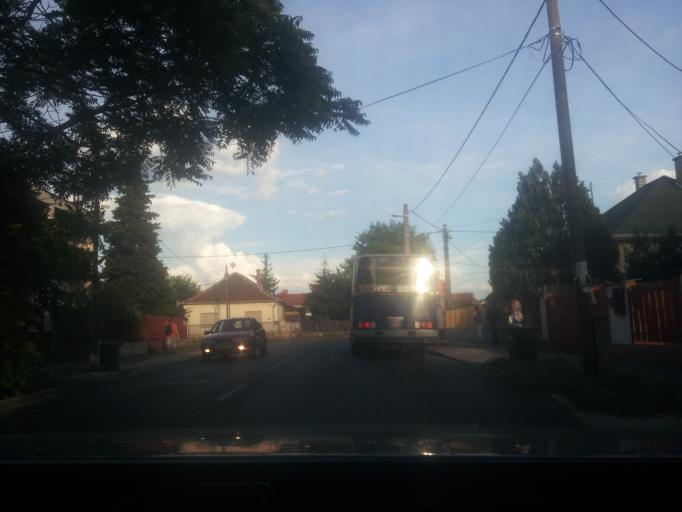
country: HU
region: Budapest
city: Budapest XVIII. keruelet
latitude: 47.4325
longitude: 19.1653
